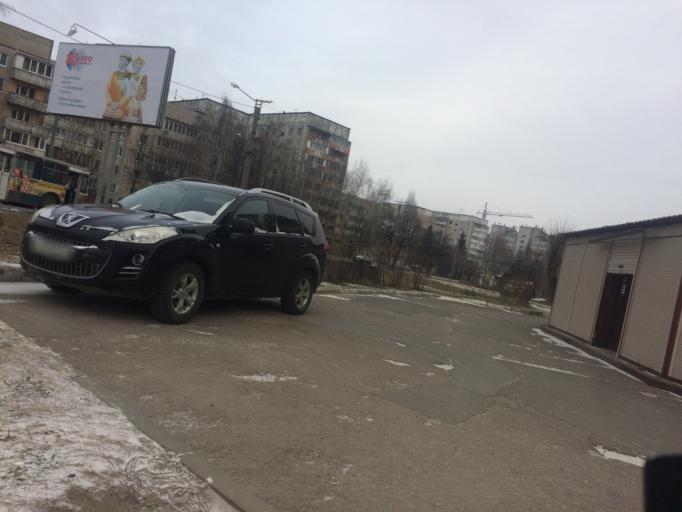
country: RU
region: Mariy-El
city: Yoshkar-Ola
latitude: 56.6449
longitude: 47.8591
